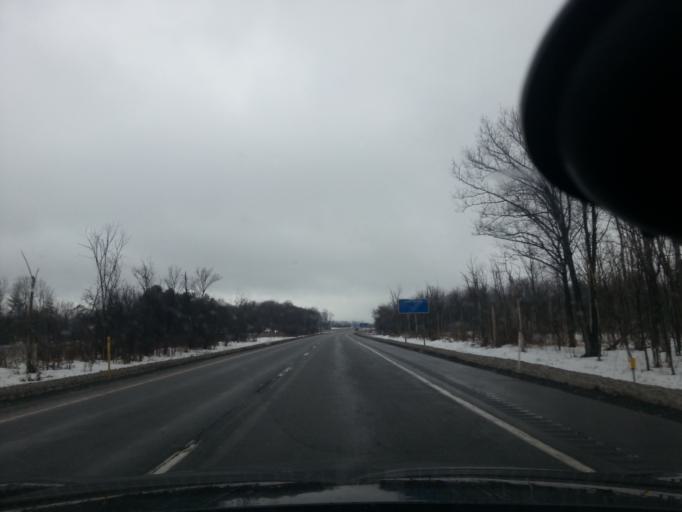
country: US
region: New York
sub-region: Jefferson County
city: Adams
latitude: 43.8234
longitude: -76.0319
